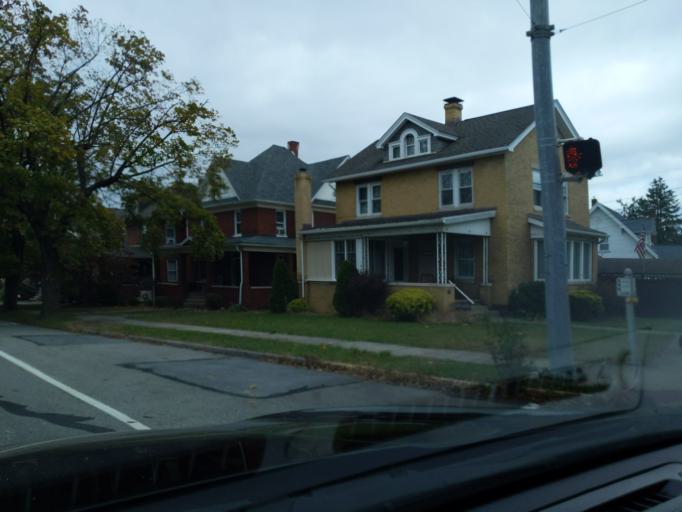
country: US
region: Pennsylvania
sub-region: Blair County
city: Hollidaysburg
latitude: 40.4352
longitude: -78.3919
